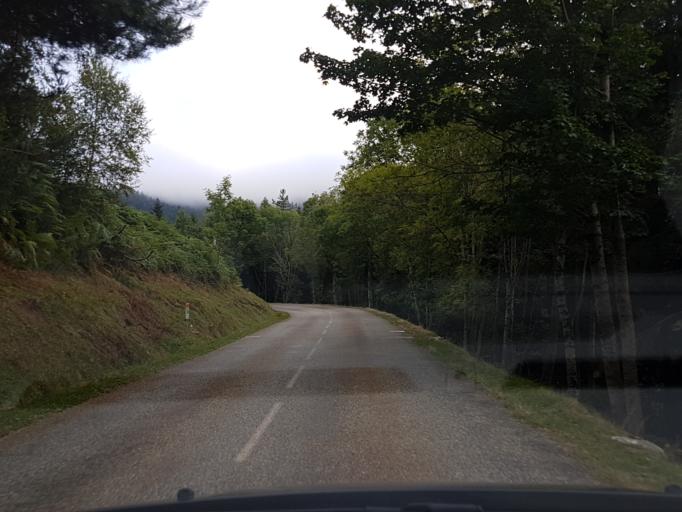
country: FR
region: Midi-Pyrenees
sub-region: Departement de l'Ariege
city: Foix
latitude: 42.9026
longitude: 1.4453
